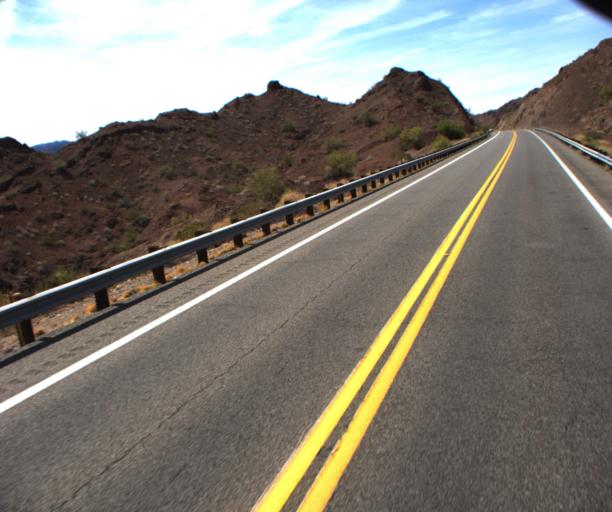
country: US
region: Arizona
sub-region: La Paz County
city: Cienega Springs
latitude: 34.3184
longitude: -114.1151
